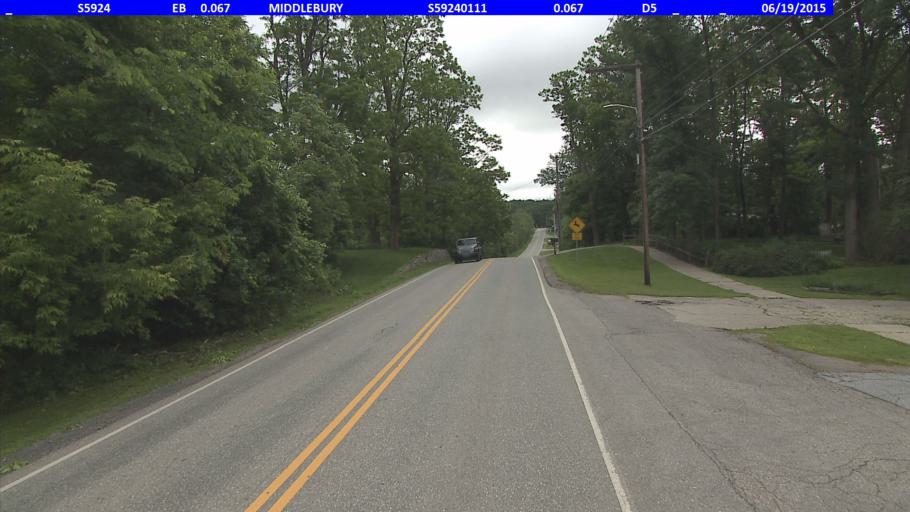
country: US
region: Vermont
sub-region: Addison County
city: Middlebury (village)
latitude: 44.0166
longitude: -73.1596
